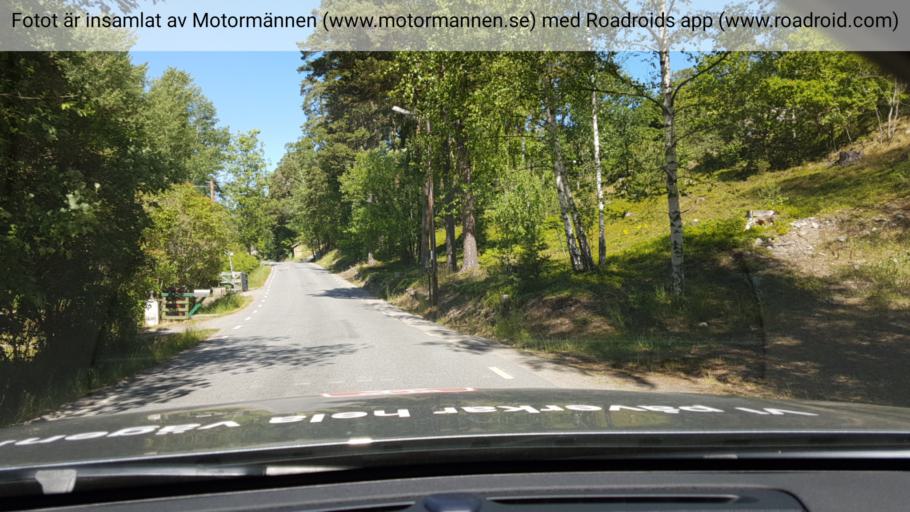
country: SE
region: Stockholm
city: Dalaro
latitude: 59.1469
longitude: 18.4346
